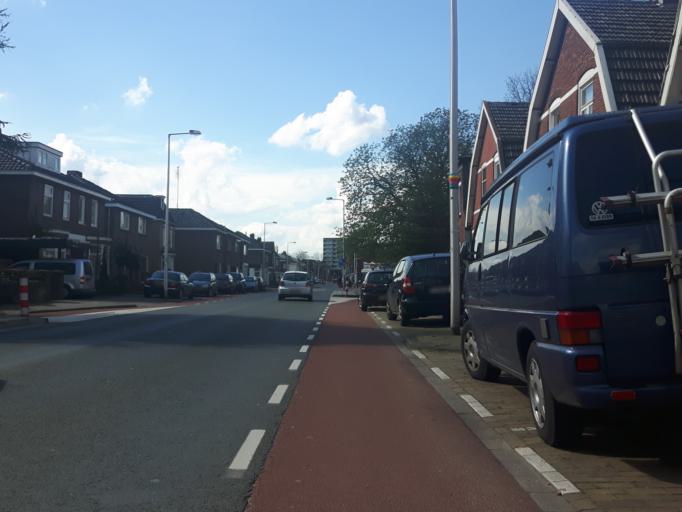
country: NL
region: Overijssel
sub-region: Gemeente Enschede
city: Enschede
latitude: 52.2277
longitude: 6.8674
